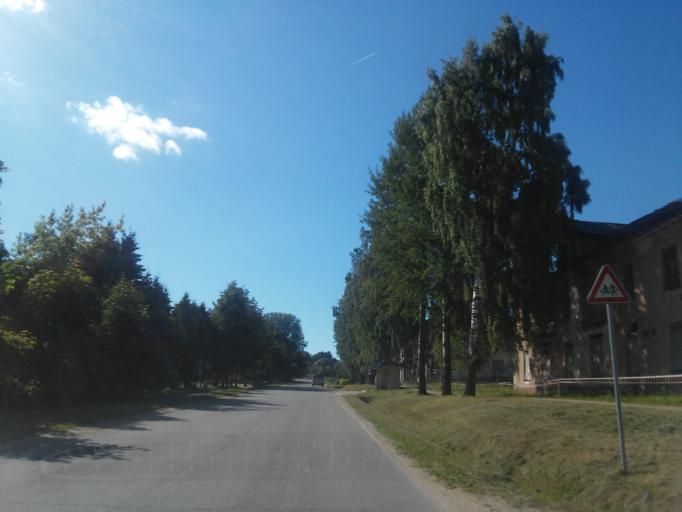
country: LV
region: Vainode
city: Vainode
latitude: 56.4172
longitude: 21.8467
